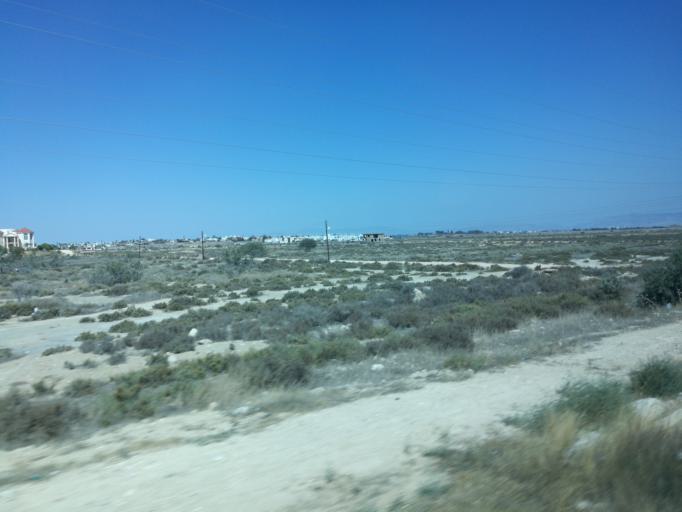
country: CY
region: Ammochostos
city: Famagusta
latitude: 35.1619
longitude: 33.8995
